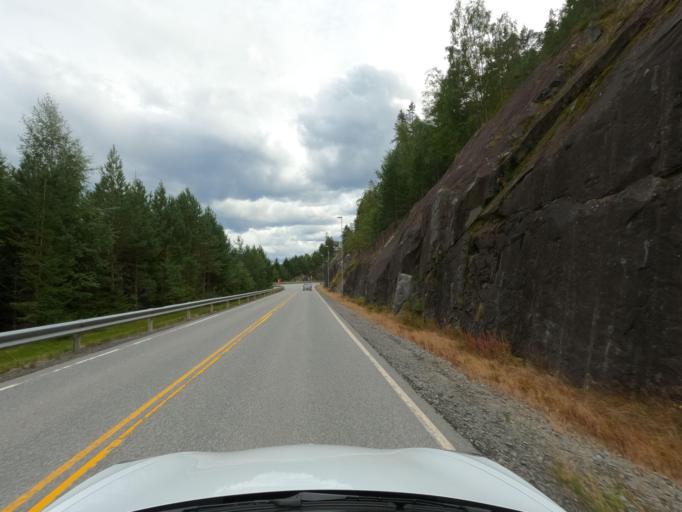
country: NO
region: Telemark
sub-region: Hjartdal
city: Sauland
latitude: 59.8972
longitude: 8.8984
